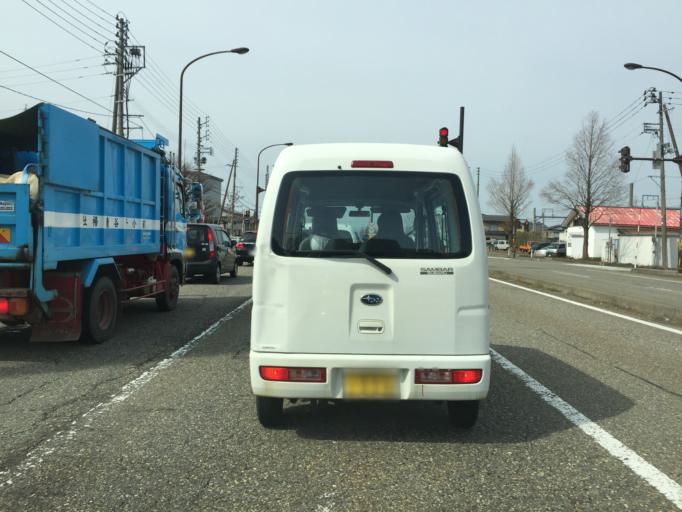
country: JP
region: Niigata
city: Ojiya
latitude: 37.3708
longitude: 138.8345
